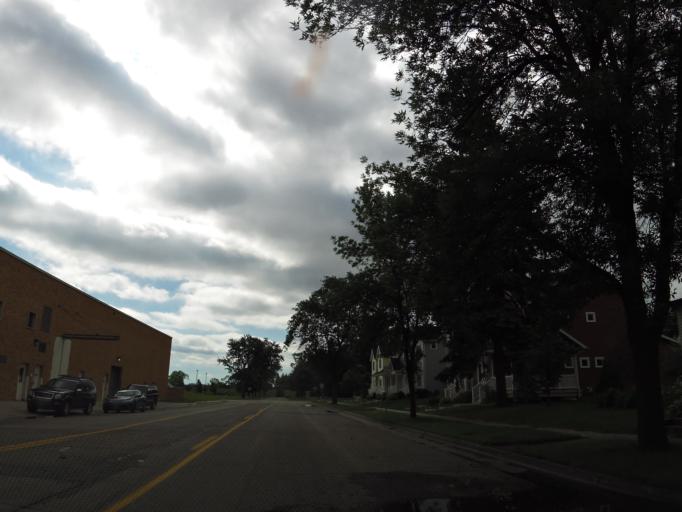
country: US
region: North Dakota
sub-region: Grand Forks County
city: Grand Forks
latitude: 47.9207
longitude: -97.0250
